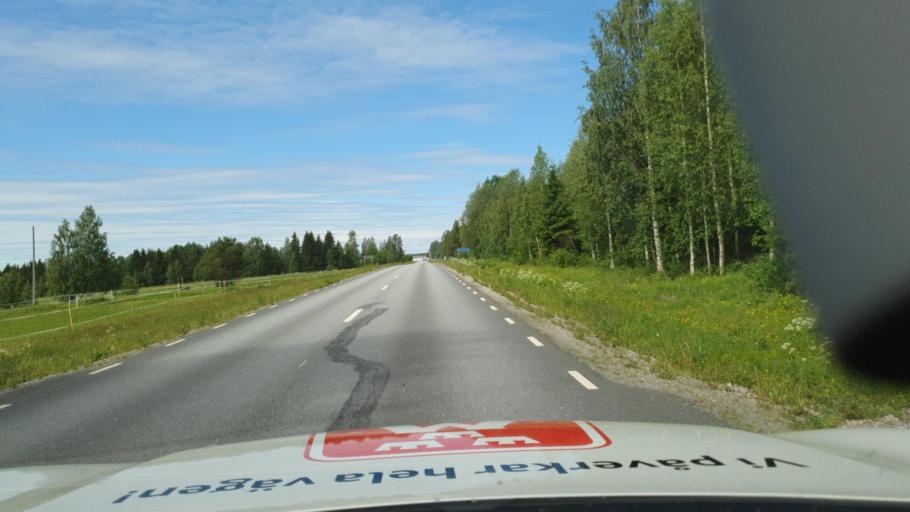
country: SE
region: Vaesterbotten
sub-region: Skelleftea Kommun
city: Forsbacka
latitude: 64.7008
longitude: 20.4625
